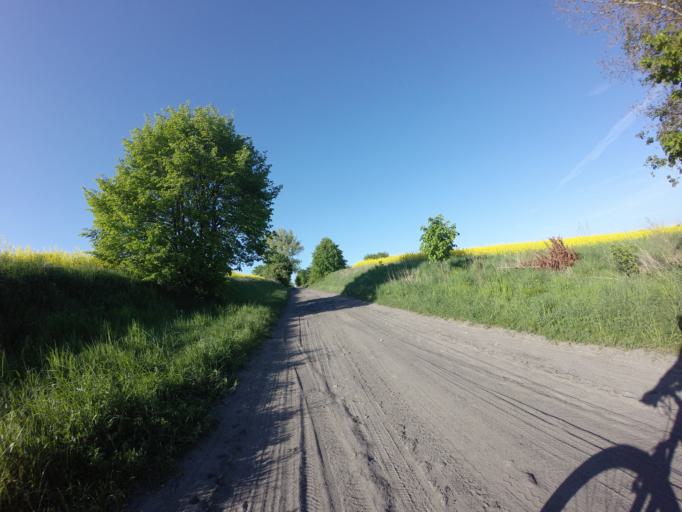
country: PL
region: West Pomeranian Voivodeship
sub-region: Powiat choszczenski
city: Choszczno
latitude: 53.1253
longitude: 15.3718
